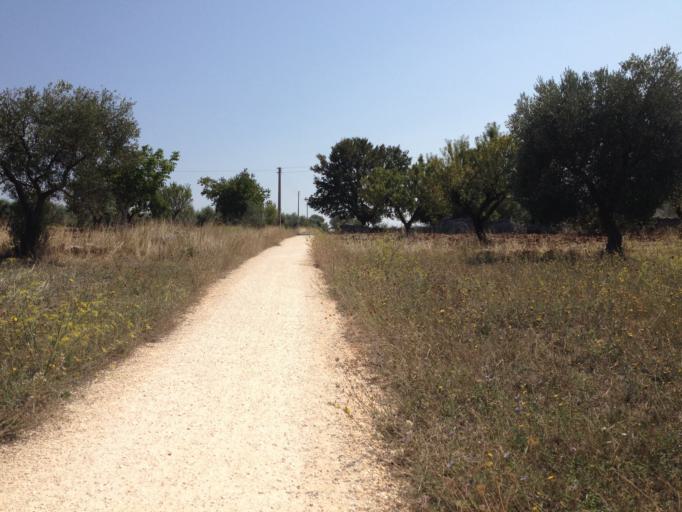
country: IT
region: Apulia
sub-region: Provincia di Brindisi
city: Cisternino
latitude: 40.7162
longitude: 17.4059
